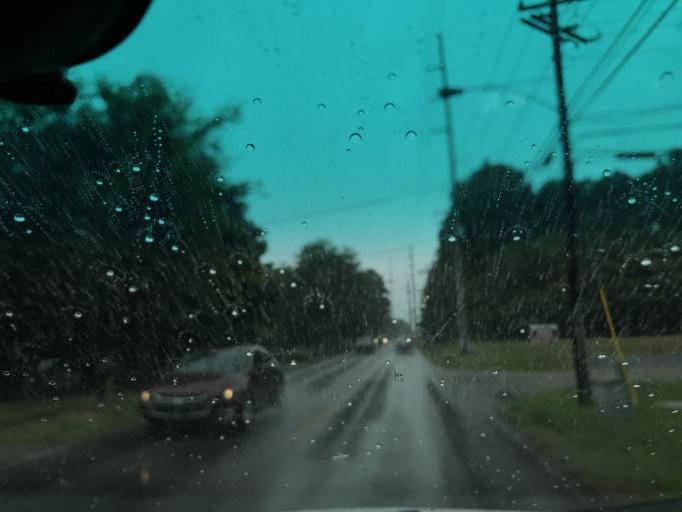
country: US
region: Alabama
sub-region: Montgomery County
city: Montgomery
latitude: 32.3670
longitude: -86.2616
